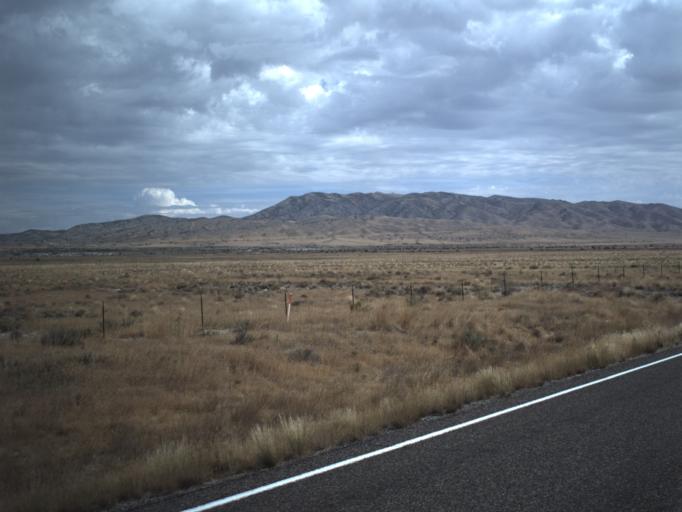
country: US
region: Utah
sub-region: Tooele County
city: Wendover
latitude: 41.4321
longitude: -113.7883
